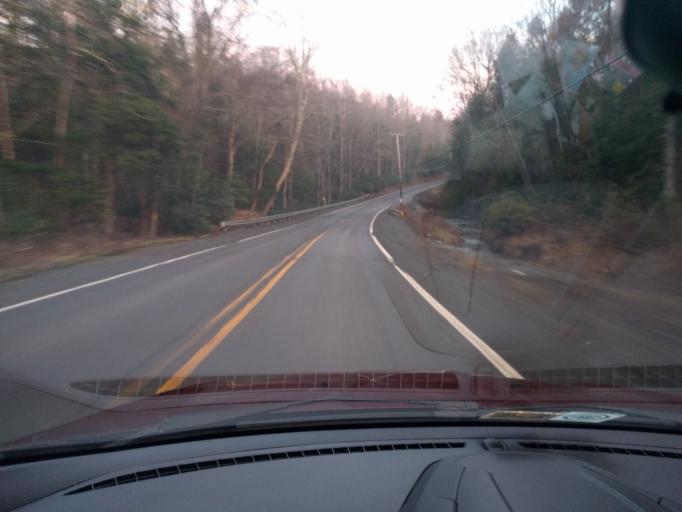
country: US
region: West Virginia
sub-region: Greenbrier County
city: Rainelle
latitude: 38.0387
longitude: -80.9215
